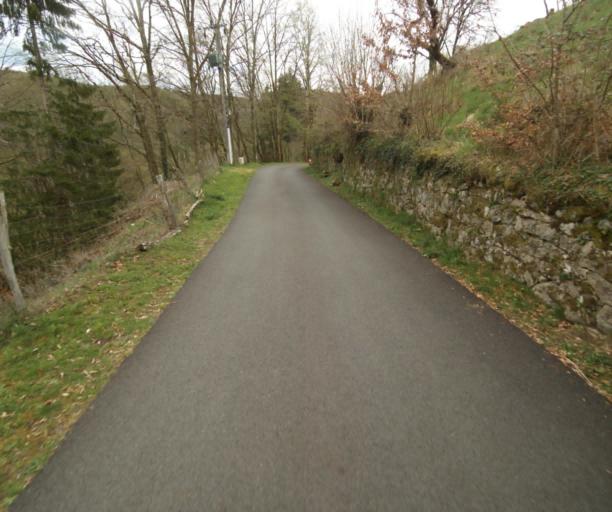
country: FR
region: Limousin
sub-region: Departement de la Correze
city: Argentat
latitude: 45.1963
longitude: 1.9746
